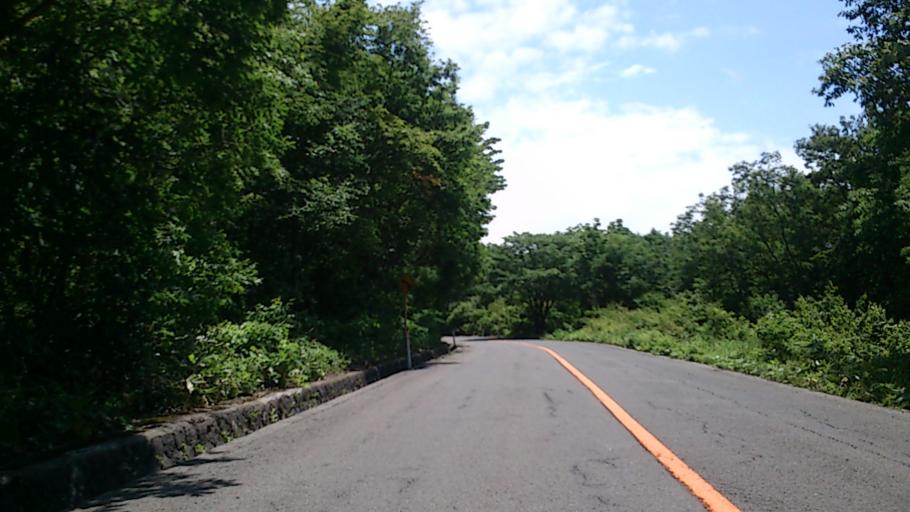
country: JP
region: Yamagata
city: Yamagata-shi
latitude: 38.1226
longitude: 140.3979
